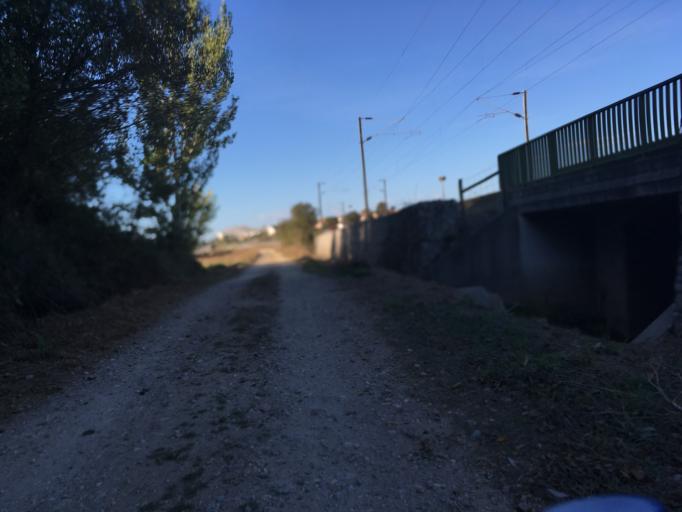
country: PT
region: Aveiro
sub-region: Estarreja
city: Salreu
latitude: 40.7239
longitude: -8.5643
